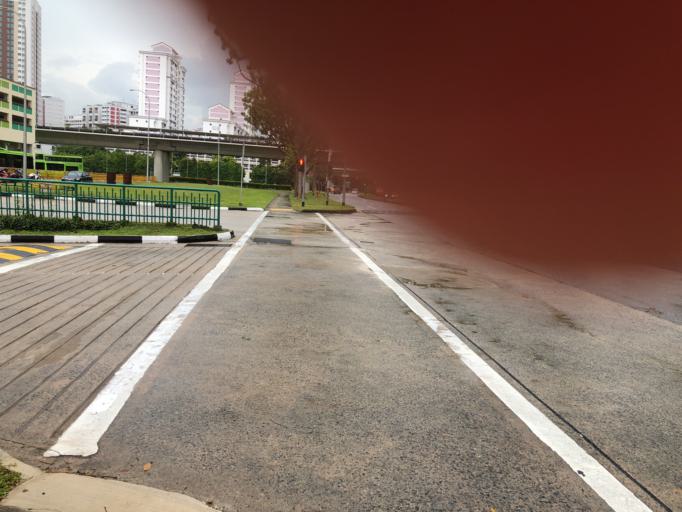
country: SG
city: Singapore
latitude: 1.3501
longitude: 103.7517
